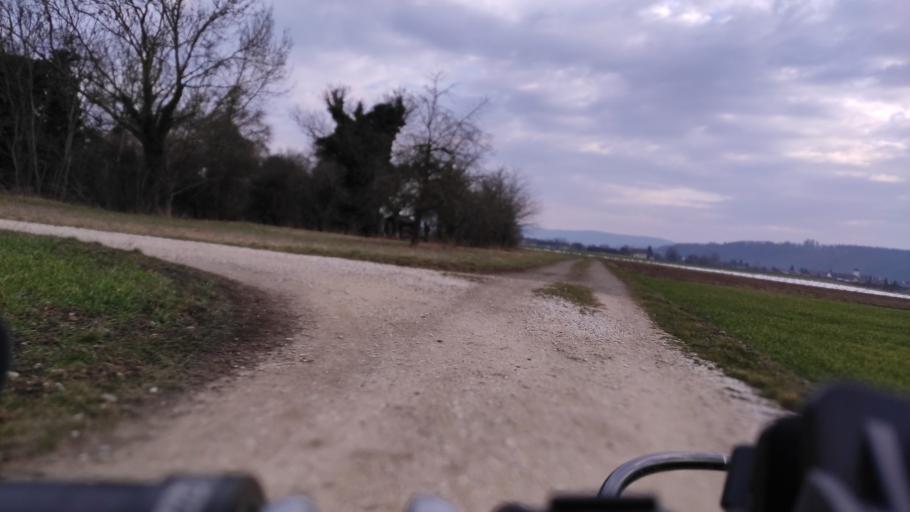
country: CH
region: Schaffhausen
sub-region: Bezirk Stein
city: Ramsen
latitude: 47.7169
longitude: 8.8154
